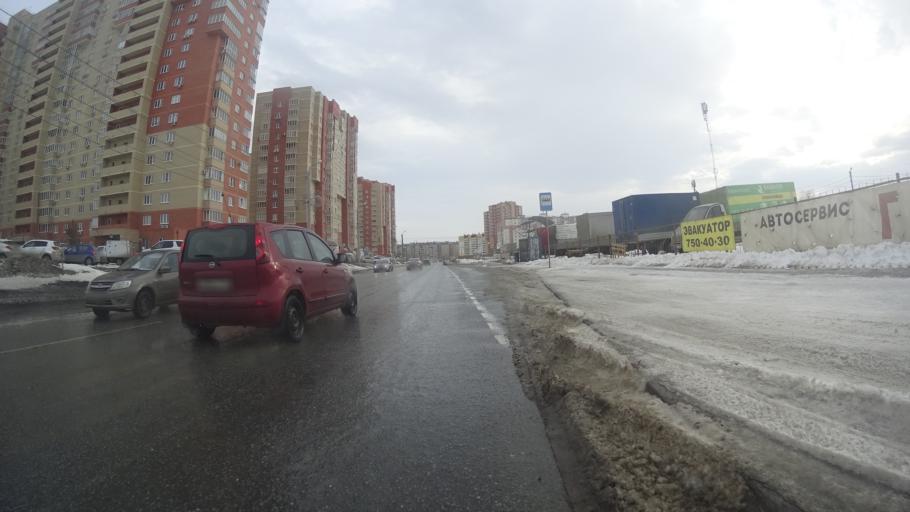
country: RU
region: Chelyabinsk
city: Roshchino
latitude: 55.1958
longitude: 61.2802
